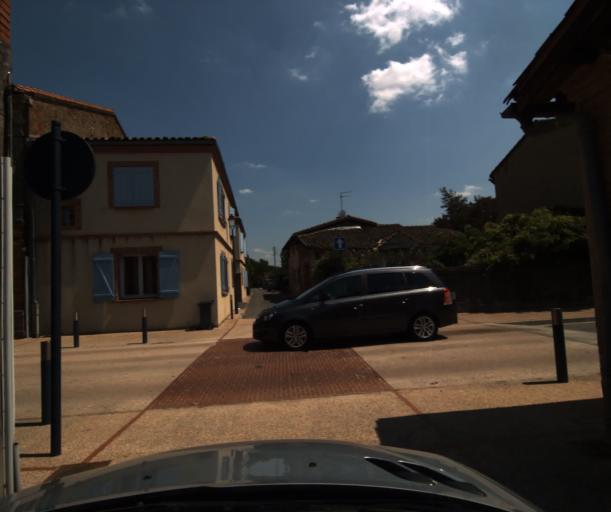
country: FR
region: Midi-Pyrenees
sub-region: Departement de la Haute-Garonne
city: Saint-Lys
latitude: 43.5121
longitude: 1.1746
